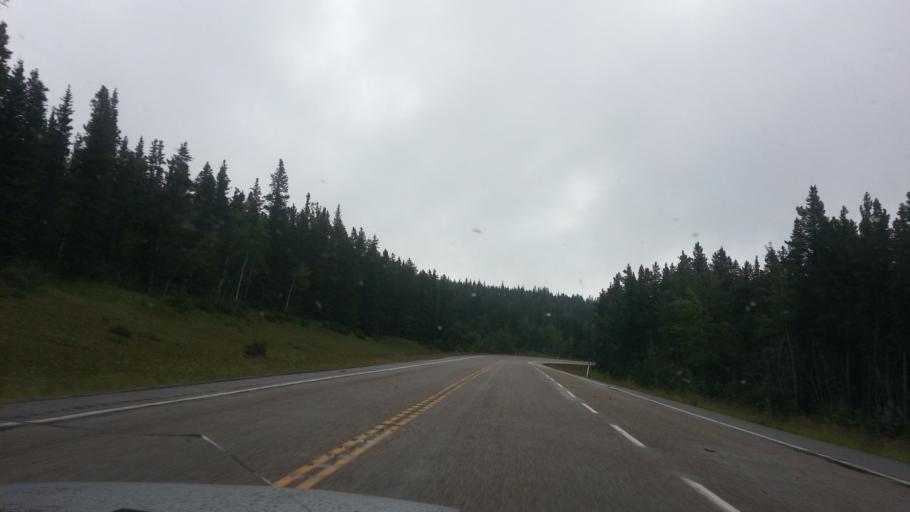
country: CA
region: Alberta
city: Cochrane
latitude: 50.8692
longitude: -114.7690
